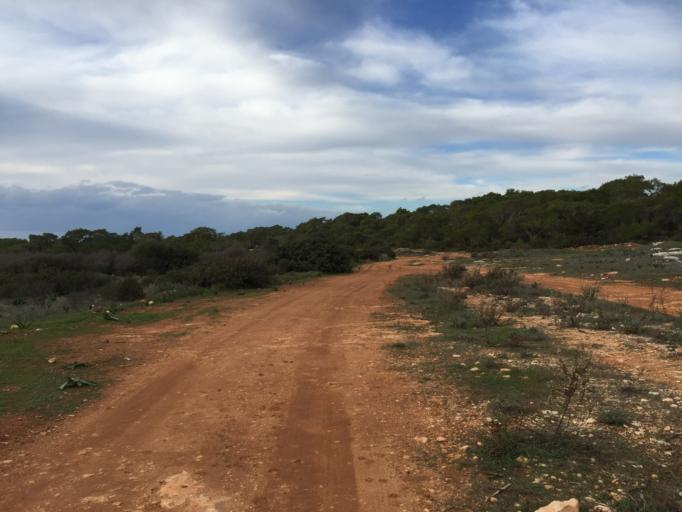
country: CY
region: Pafos
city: Pegeia
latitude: 34.8936
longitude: 32.3724
